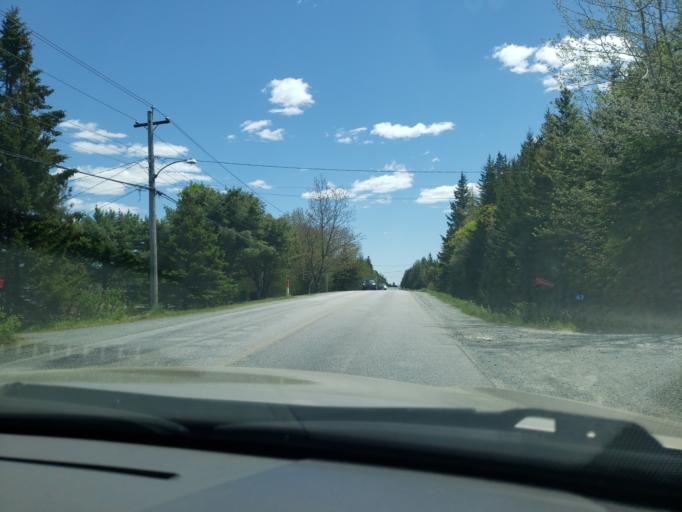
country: CA
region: Nova Scotia
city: Cole Harbour
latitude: 44.7359
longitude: -63.3103
